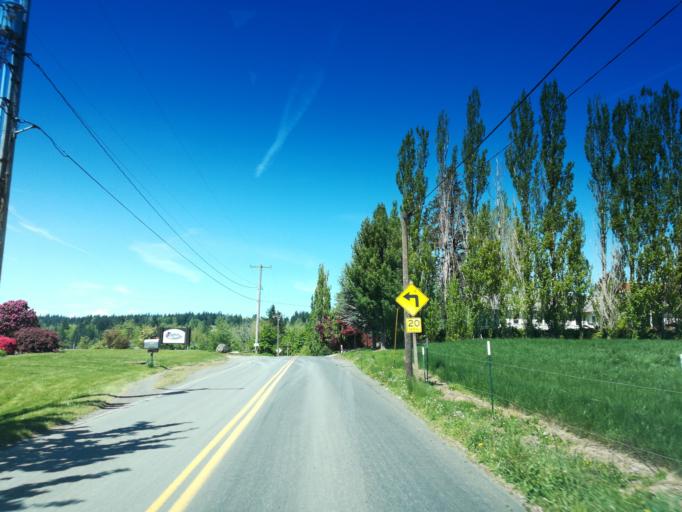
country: US
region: Oregon
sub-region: Multnomah County
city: Troutdale
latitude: 45.5111
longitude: -122.3521
